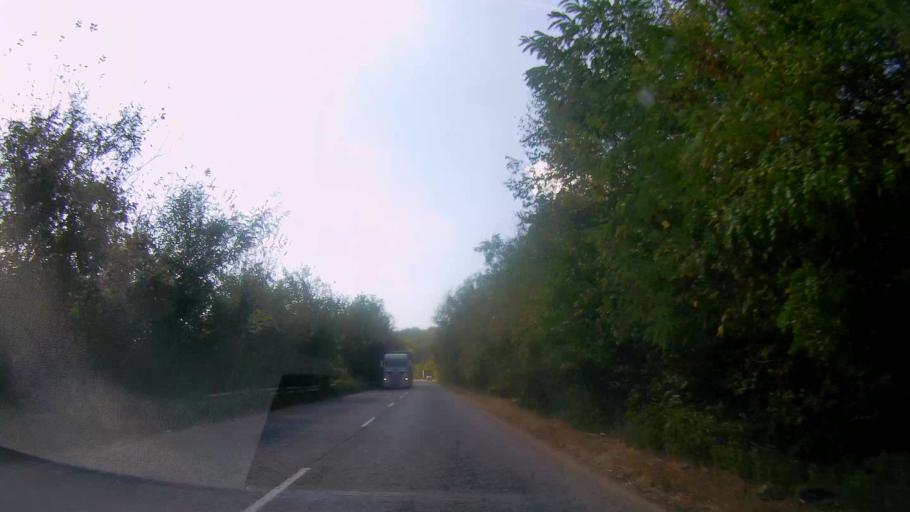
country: BG
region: Veliko Turnovo
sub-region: Obshtina Polski Trumbesh
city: Polski Trumbesh
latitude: 43.4419
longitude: 25.6552
